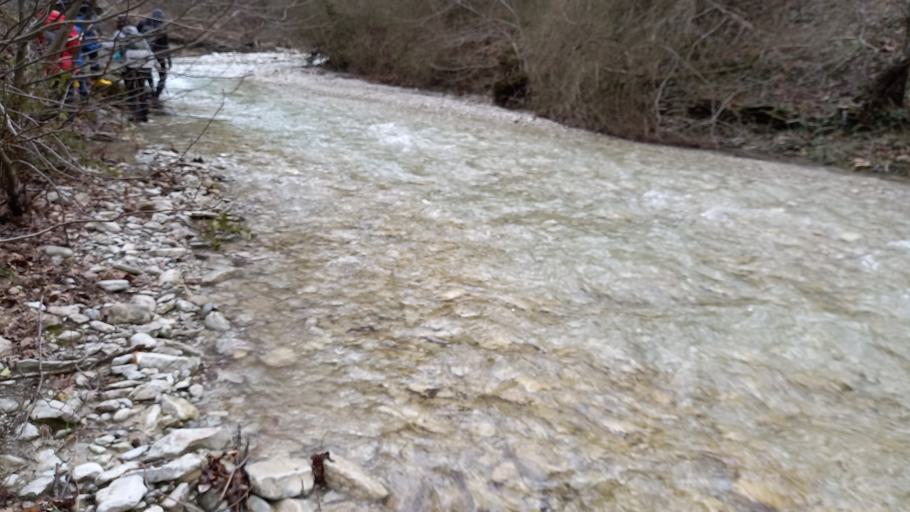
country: RU
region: Krasnodarskiy
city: Dzhubga
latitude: 44.4049
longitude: 38.7105
